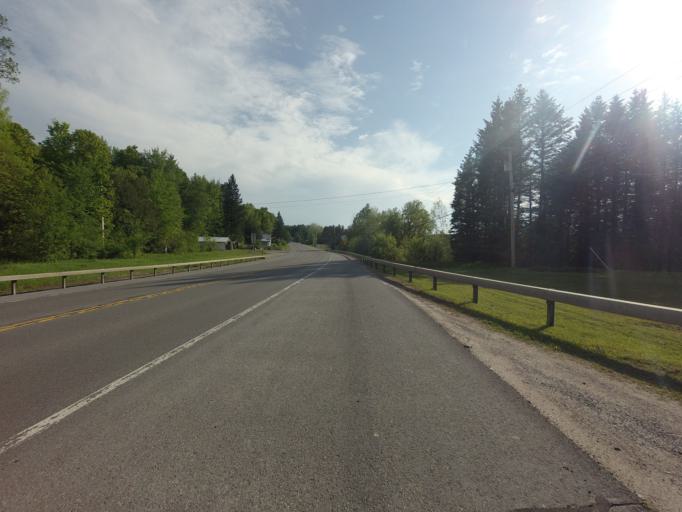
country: US
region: New York
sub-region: St. Lawrence County
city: Gouverneur
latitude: 44.1627
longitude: -75.3134
